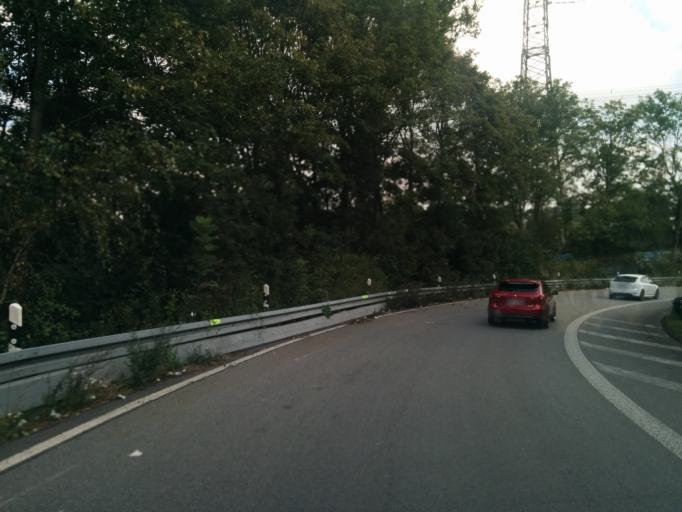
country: DE
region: North Rhine-Westphalia
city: Waltrop
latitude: 51.5869
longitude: 7.3682
